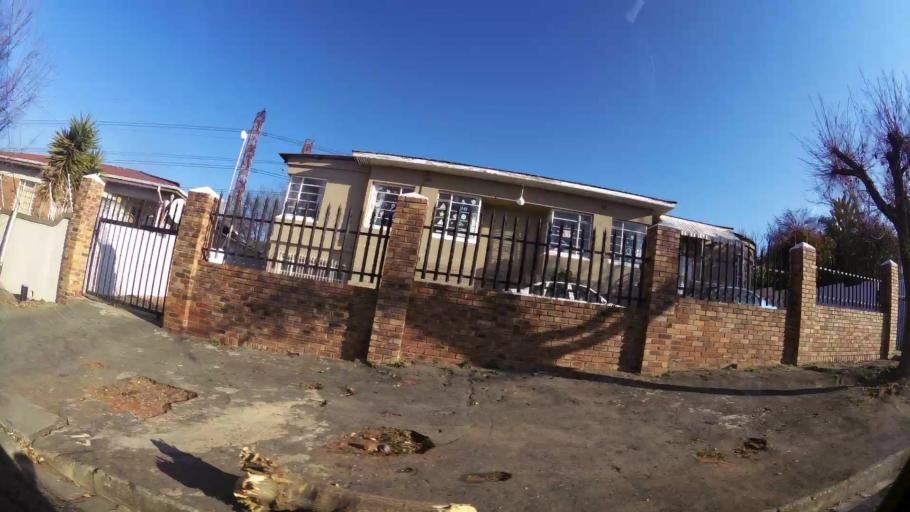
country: ZA
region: Gauteng
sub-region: Ekurhuleni Metropolitan Municipality
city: Germiston
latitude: -26.1905
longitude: 28.1470
